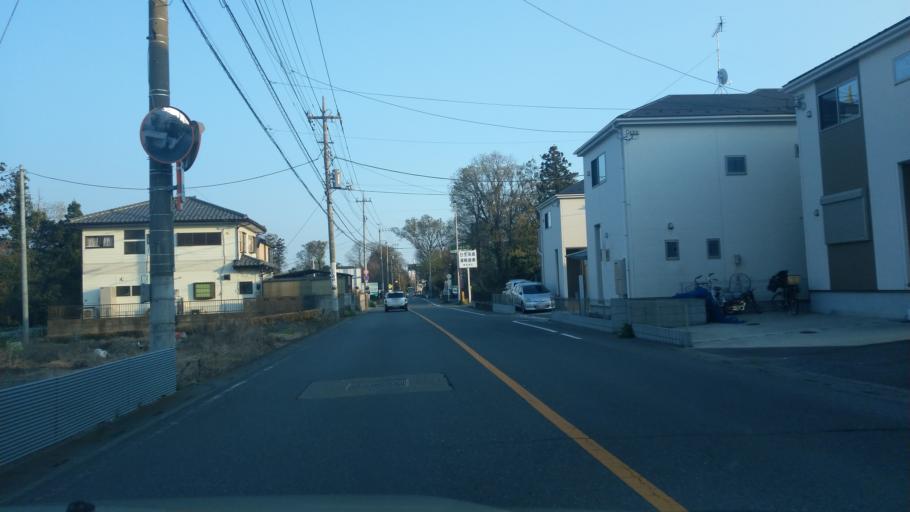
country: JP
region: Saitama
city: Ageoshimo
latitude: 35.9925
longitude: 139.6038
